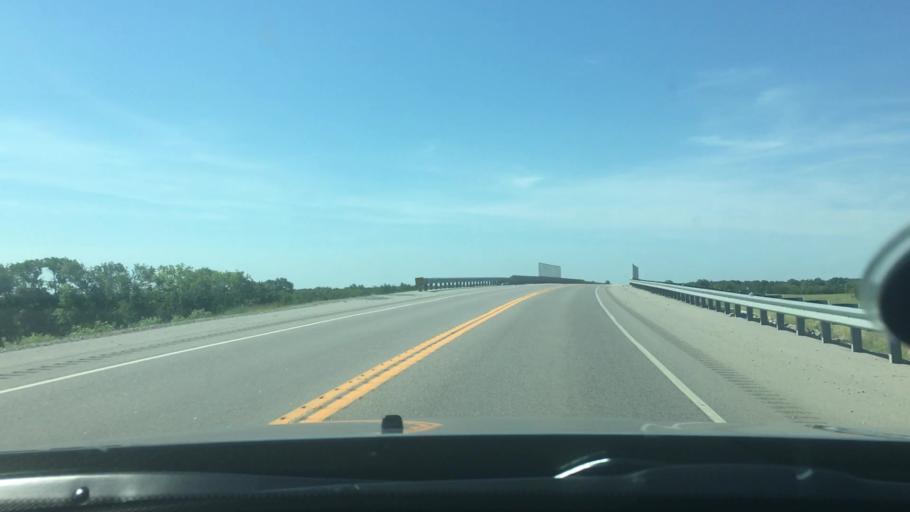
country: US
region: Oklahoma
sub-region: Bryan County
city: Durant
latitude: 33.9770
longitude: -96.3398
